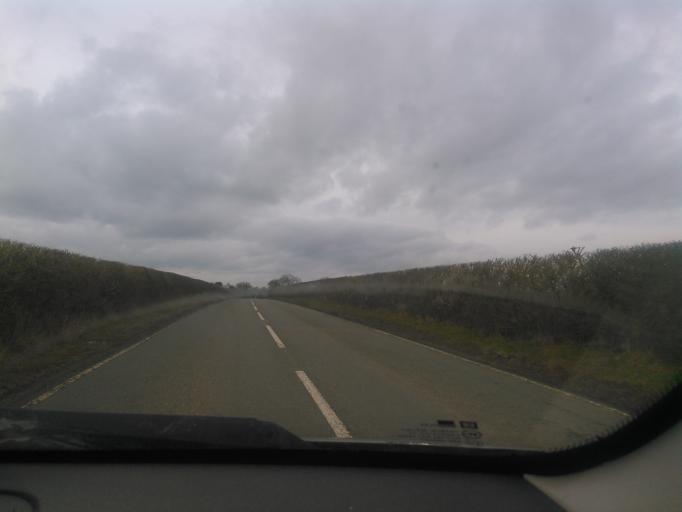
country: GB
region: England
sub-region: Shropshire
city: Wem
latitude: 52.8331
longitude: -2.6976
